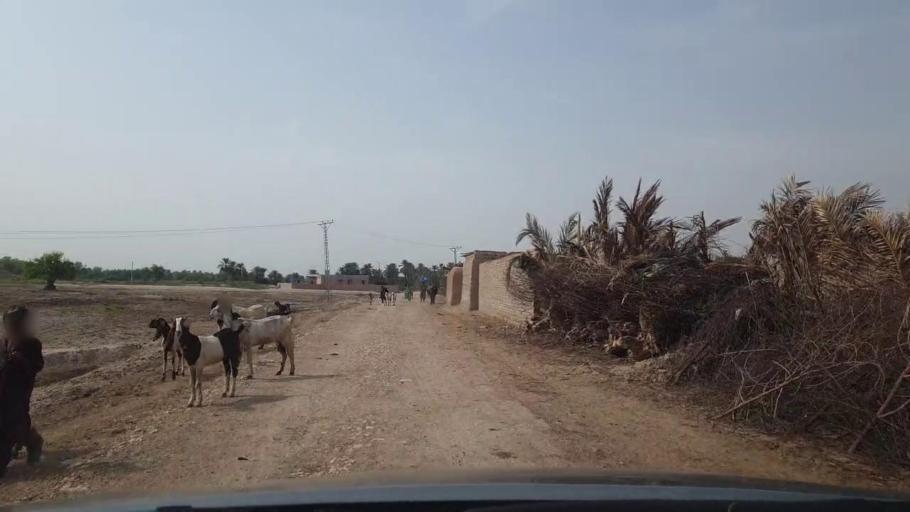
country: PK
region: Sindh
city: Rohri
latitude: 27.6621
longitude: 69.0132
